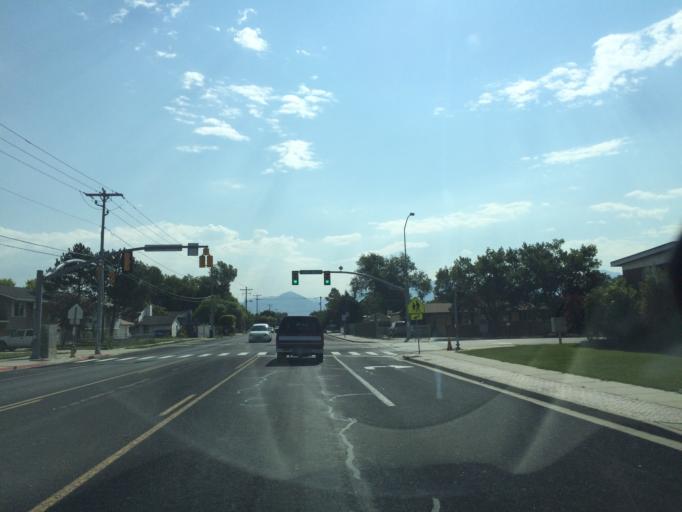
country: US
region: Utah
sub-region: Salt Lake County
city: West Valley City
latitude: 40.7039
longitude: -111.9969
